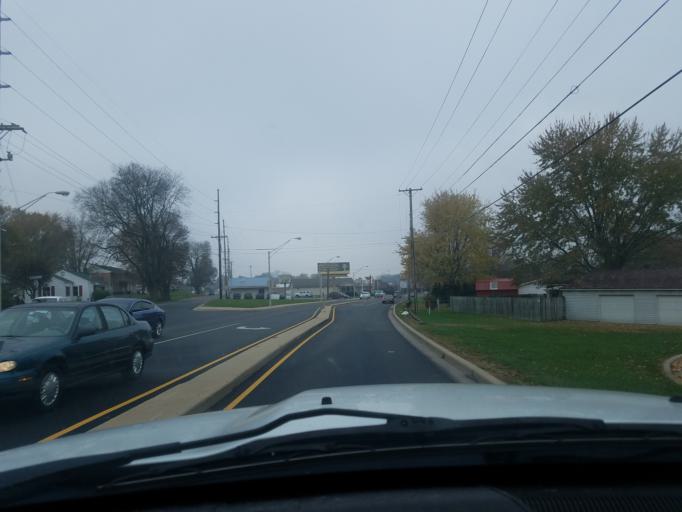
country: US
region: Indiana
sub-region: Cass County
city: Logansport
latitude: 40.7573
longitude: -86.3241
